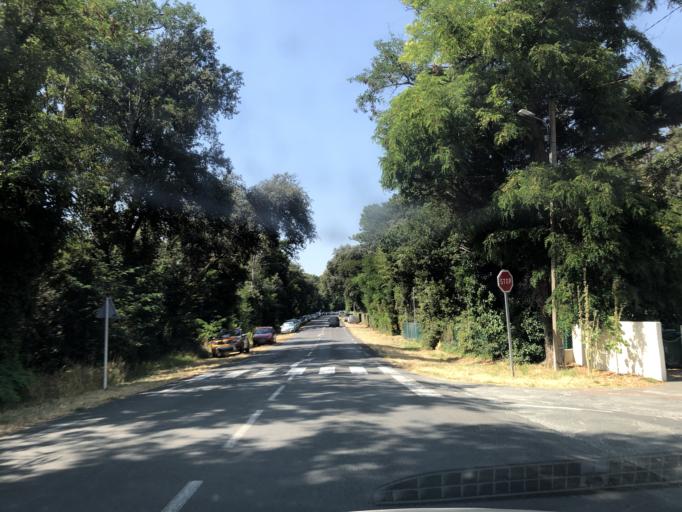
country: FR
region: Poitou-Charentes
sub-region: Departement de la Charente-Maritime
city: Meschers-sur-Gironde
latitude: 45.5656
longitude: -0.9700
